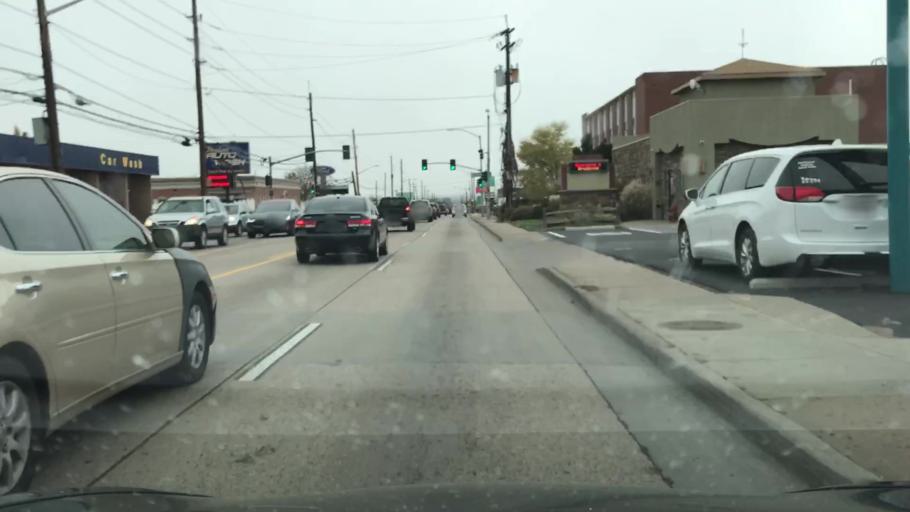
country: US
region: Colorado
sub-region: Arapahoe County
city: Glendale
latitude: 39.6785
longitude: -104.9243
